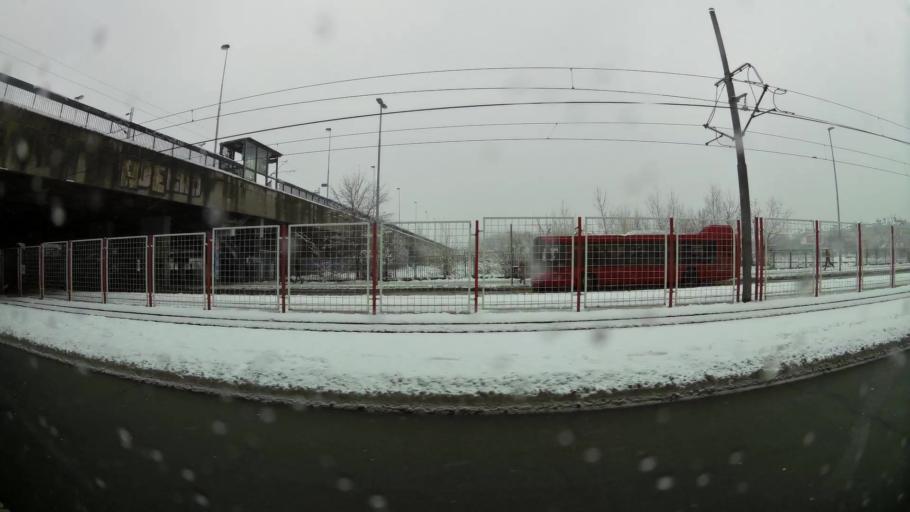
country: RS
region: Central Serbia
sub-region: Belgrade
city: Novi Beograd
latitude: 44.8071
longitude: 20.4187
